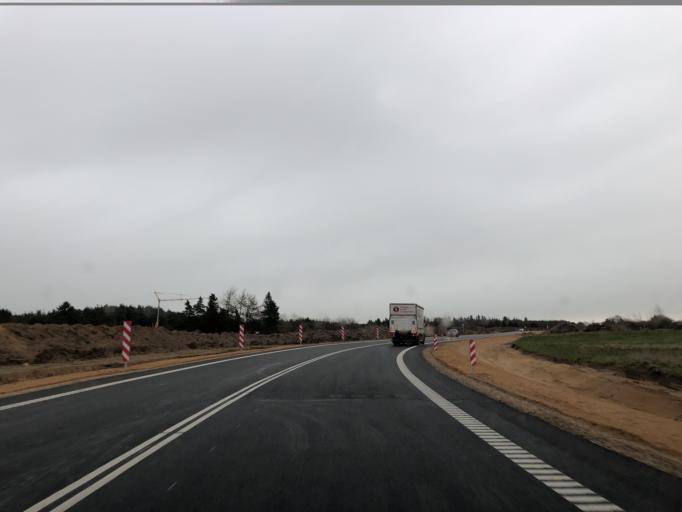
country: DK
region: Central Jutland
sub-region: Skive Kommune
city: Skive
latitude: 56.4033
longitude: 8.9641
